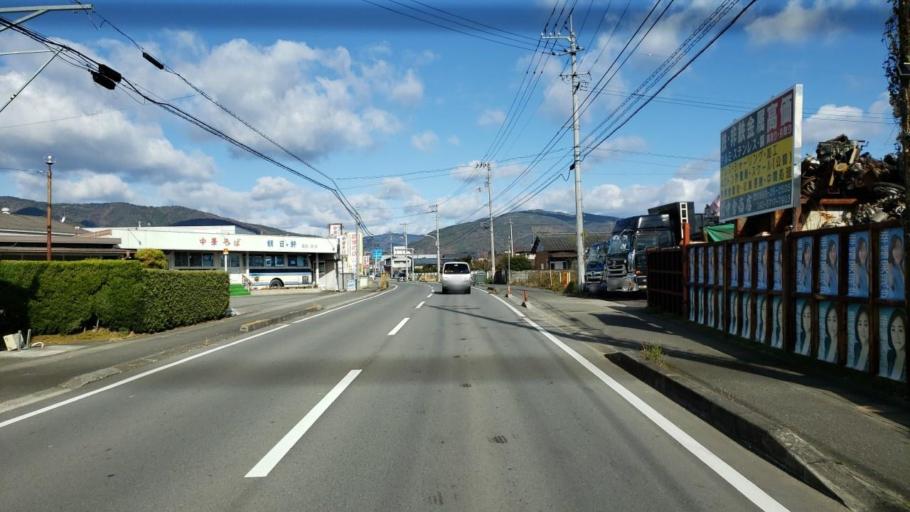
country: JP
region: Tokushima
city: Kamojimacho-jogejima
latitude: 34.0981
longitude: 134.3448
